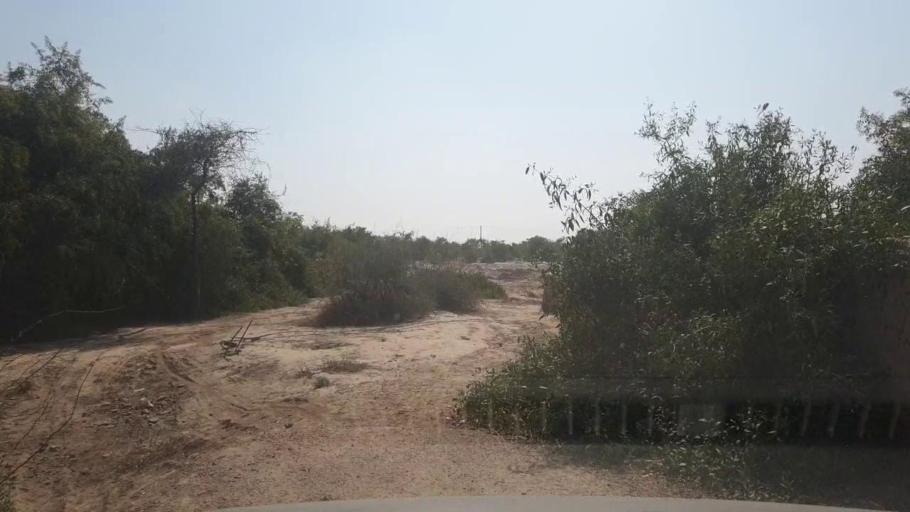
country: PK
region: Sindh
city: Chambar
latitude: 25.2242
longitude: 68.8214
